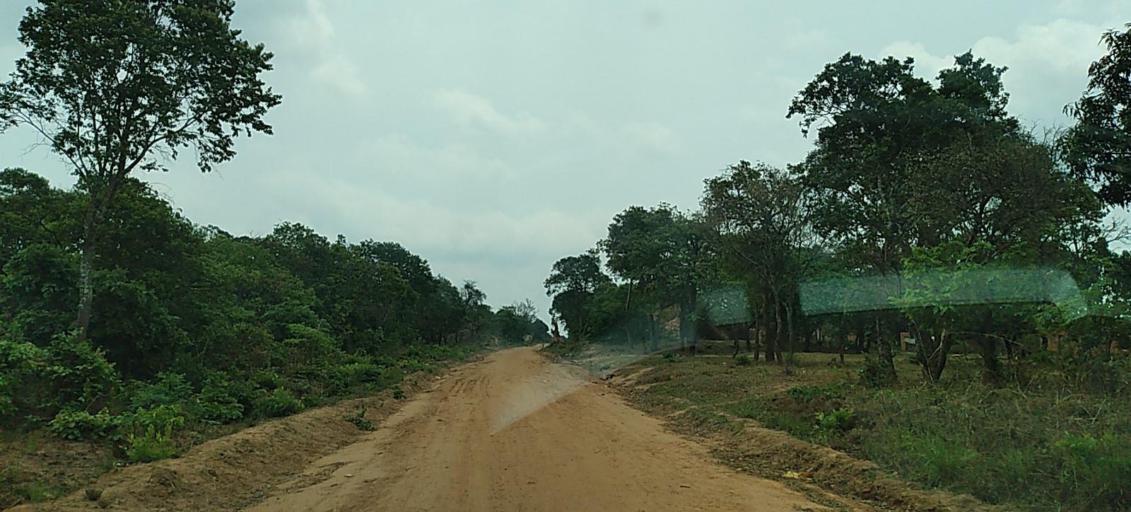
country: ZM
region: North-Western
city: Mwinilunga
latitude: -11.4529
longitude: 24.7543
